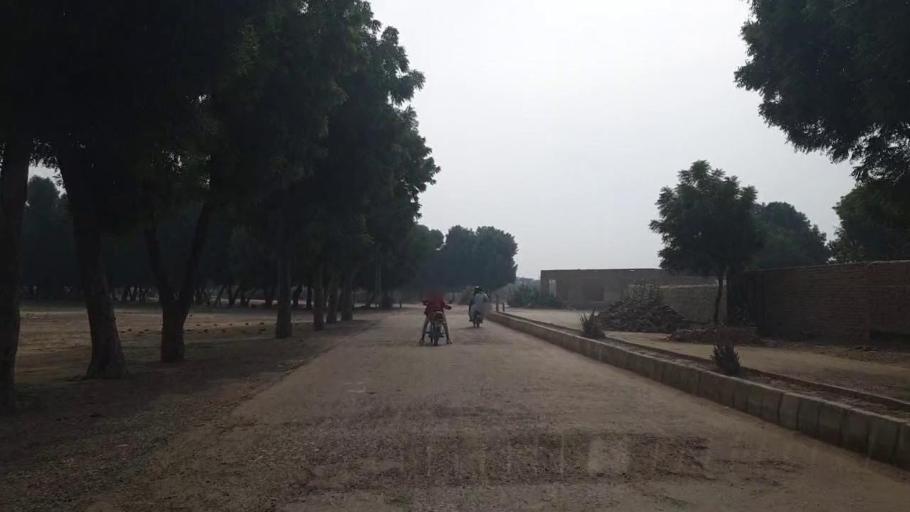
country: PK
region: Sindh
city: Sann
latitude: 26.0369
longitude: 68.1406
